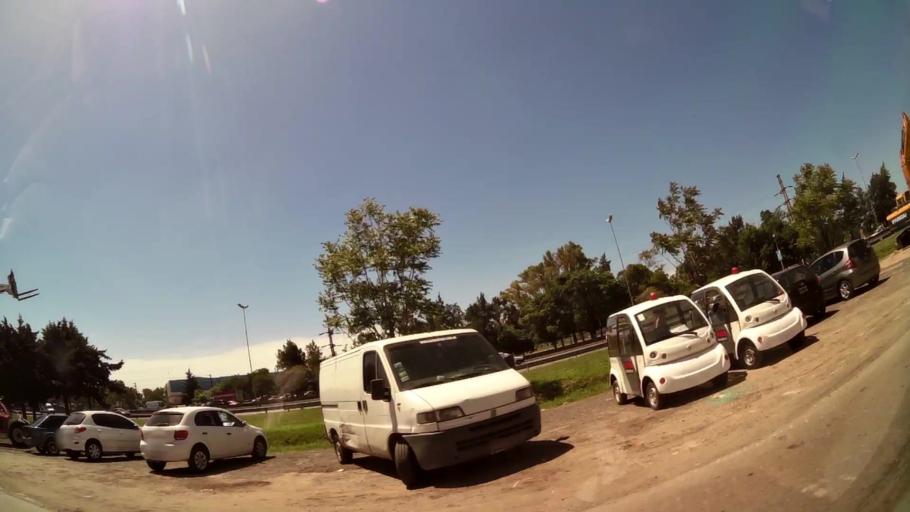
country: AR
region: Buenos Aires
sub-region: Partido de Tigre
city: Tigre
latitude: -34.4809
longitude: -58.6438
